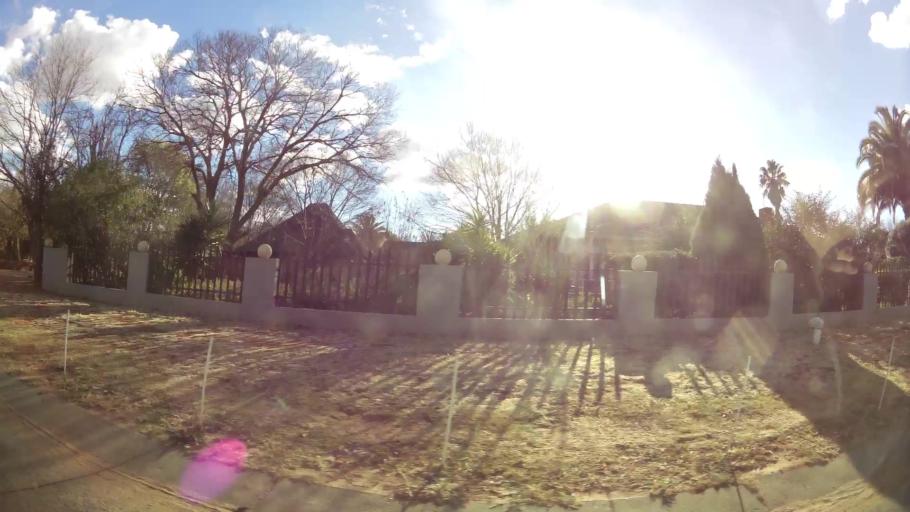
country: ZA
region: North-West
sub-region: Dr Kenneth Kaunda District Municipality
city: Klerksdorp
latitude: -26.8408
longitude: 26.6575
